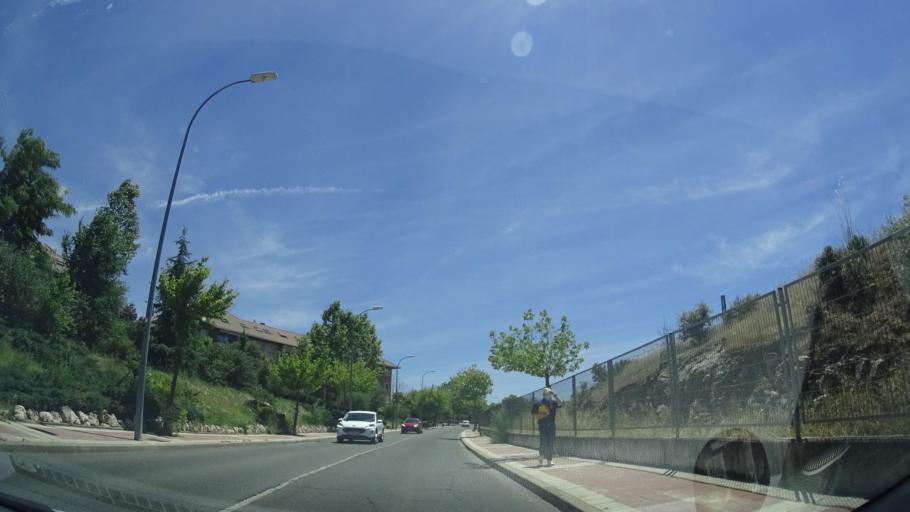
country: ES
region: Madrid
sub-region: Provincia de Madrid
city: Collado-Villalba
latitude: 40.6255
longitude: -4.0023
